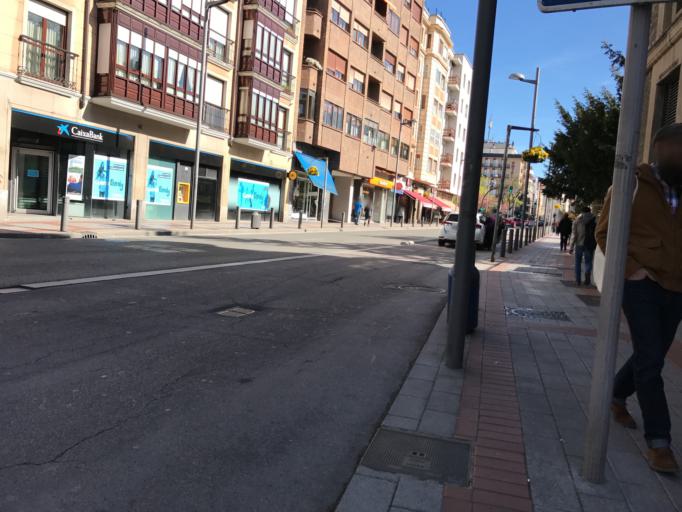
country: ES
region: Basque Country
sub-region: Provincia de Alava
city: Gasteiz / Vitoria
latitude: 42.8503
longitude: -2.6691
